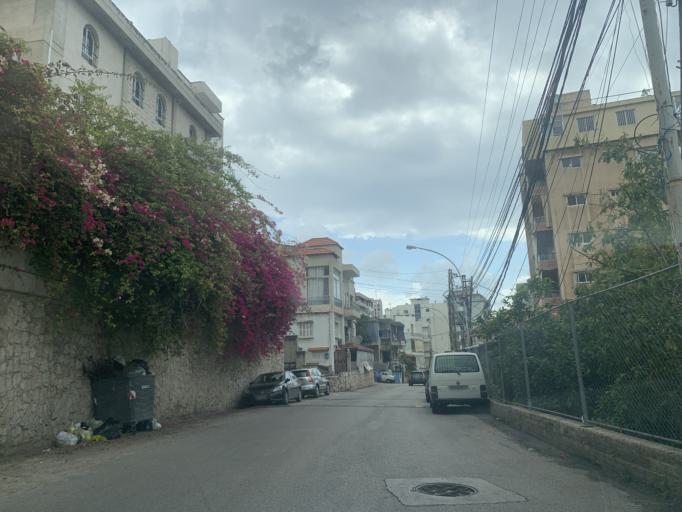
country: LB
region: Mont-Liban
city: Djounie
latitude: 33.9850
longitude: 35.6419
